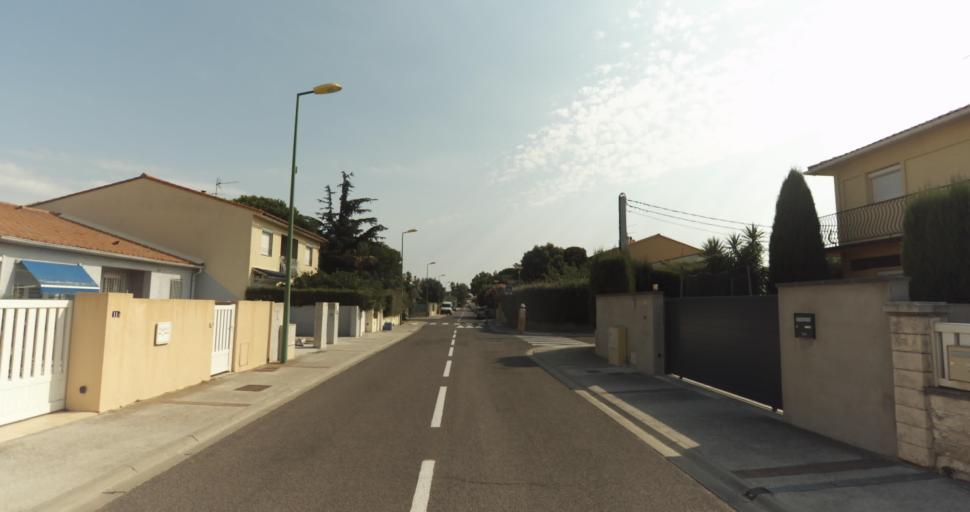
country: FR
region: Languedoc-Roussillon
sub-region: Departement des Pyrenees-Orientales
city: Latour-Bas-Elne
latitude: 42.6060
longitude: 3.0045
